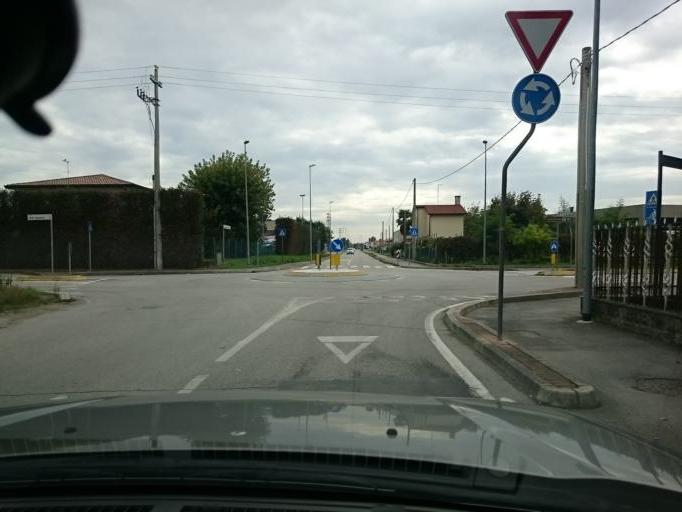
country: IT
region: Veneto
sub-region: Provincia di Padova
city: Arzergrande
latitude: 45.2885
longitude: 12.0514
